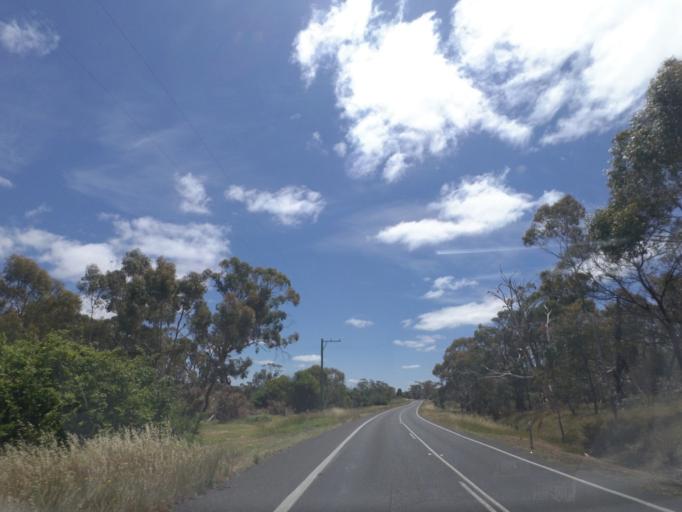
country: AU
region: Victoria
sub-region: Mount Alexander
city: Castlemaine
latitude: -37.2807
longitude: 144.1512
